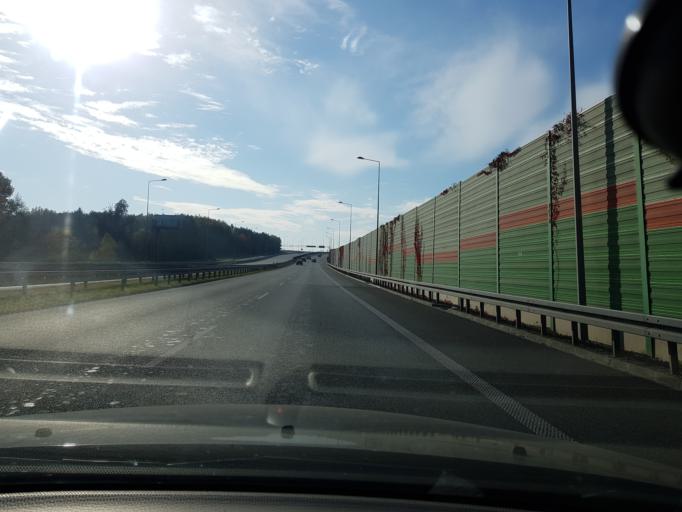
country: PL
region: Lodz Voivodeship
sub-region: Powiat rawski
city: Rawa Mazowiecka
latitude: 51.7096
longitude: 20.2190
